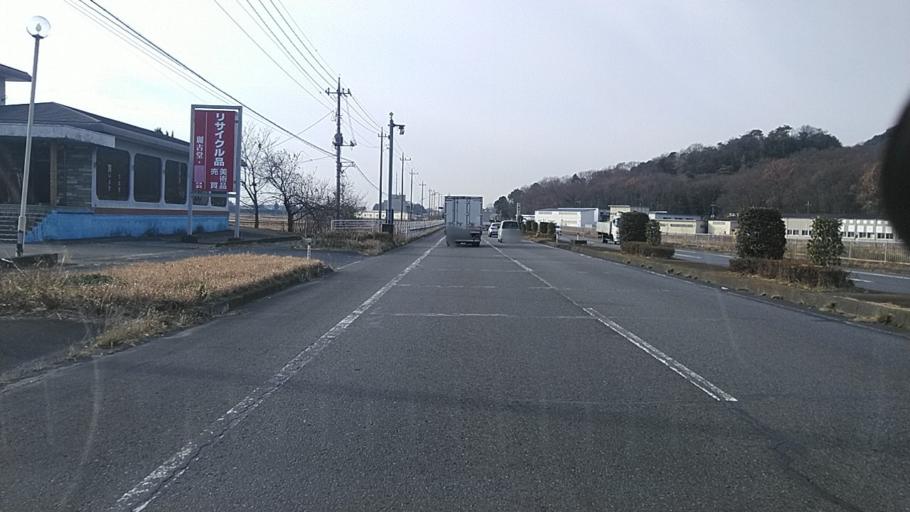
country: JP
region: Tochigi
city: Sano
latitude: 36.3039
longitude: 139.6364
